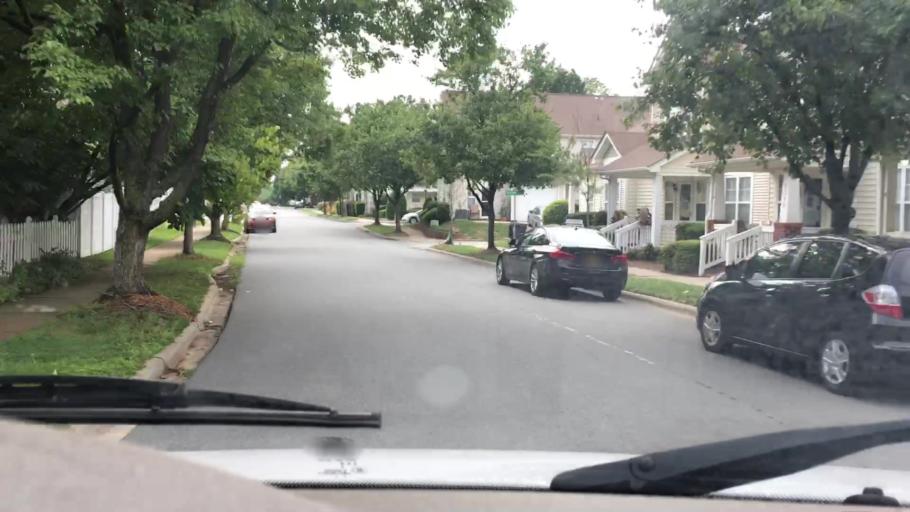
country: US
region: North Carolina
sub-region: Mecklenburg County
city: Cornelius
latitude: 35.4464
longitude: -80.8834
